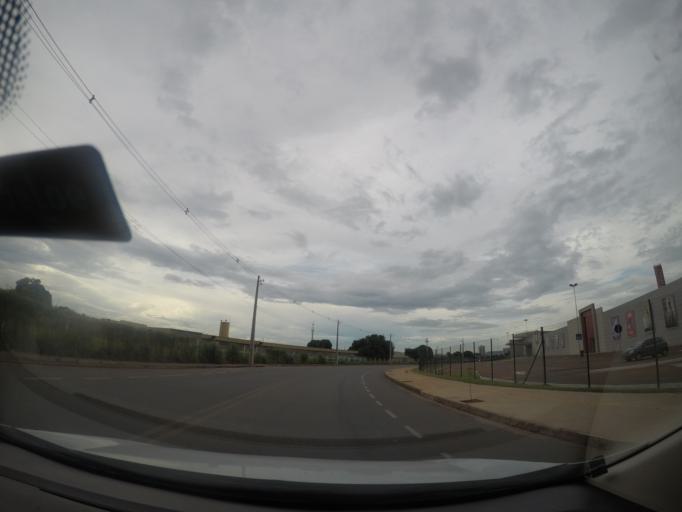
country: BR
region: Goias
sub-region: Goiania
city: Goiania
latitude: -16.6562
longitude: -49.2692
